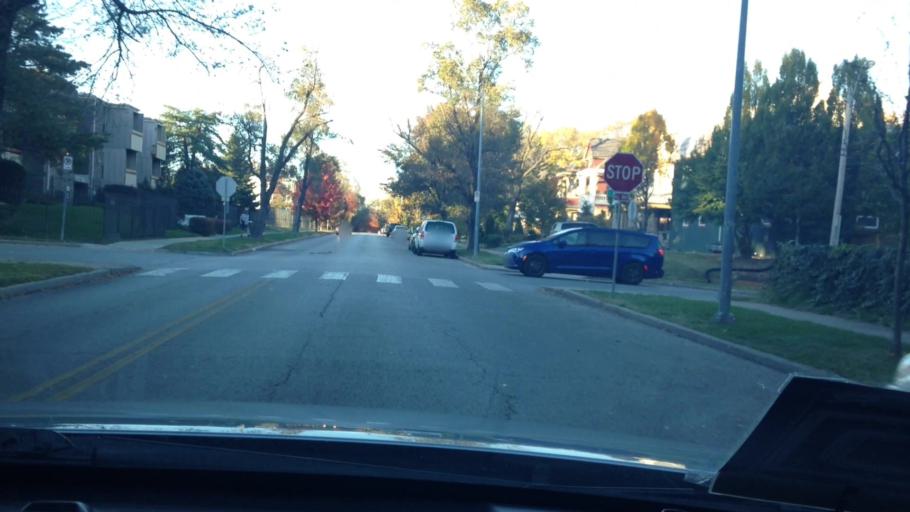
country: US
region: Kansas
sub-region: Johnson County
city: Westwood
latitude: 39.0515
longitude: -94.5841
